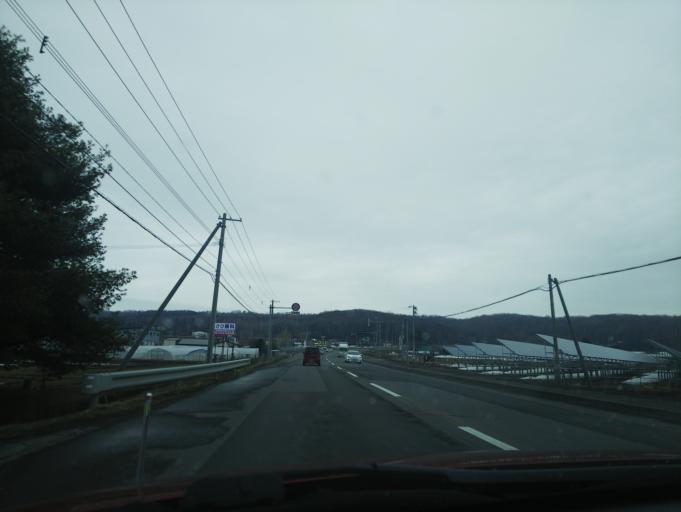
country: JP
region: Hokkaido
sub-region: Asahikawa-shi
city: Asahikawa
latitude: 43.8454
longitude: 142.4445
